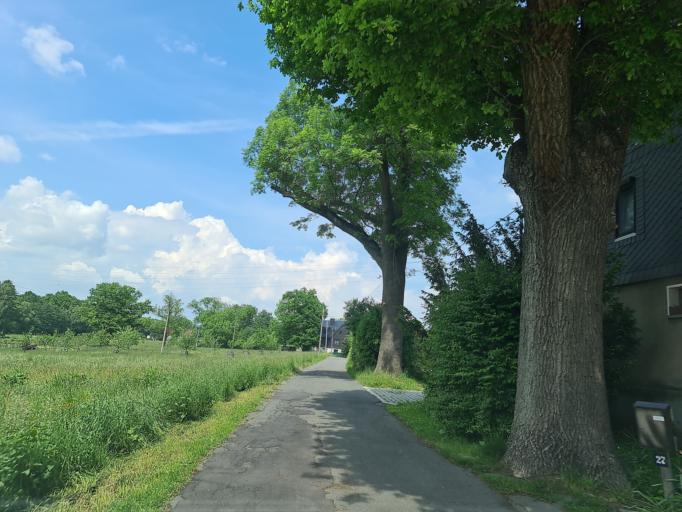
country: DE
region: Saxony
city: Lossnitz
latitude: 50.6699
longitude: 12.7404
